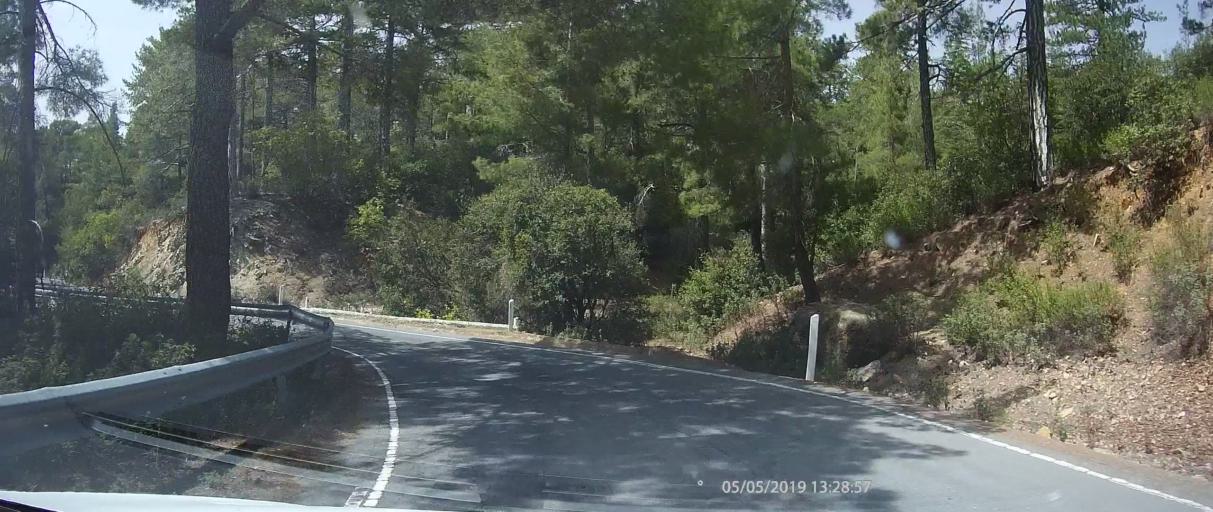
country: CY
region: Lefkosia
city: Kakopetria
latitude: 34.8972
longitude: 32.8516
